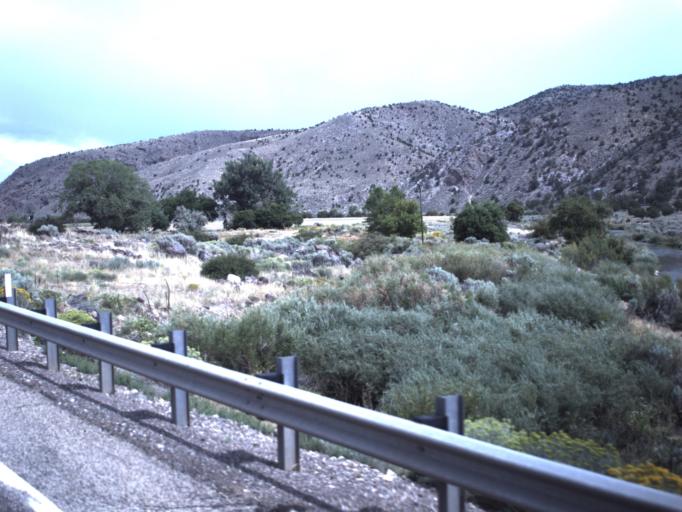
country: US
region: Utah
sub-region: Piute County
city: Junction
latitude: 38.1386
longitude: -112.3136
